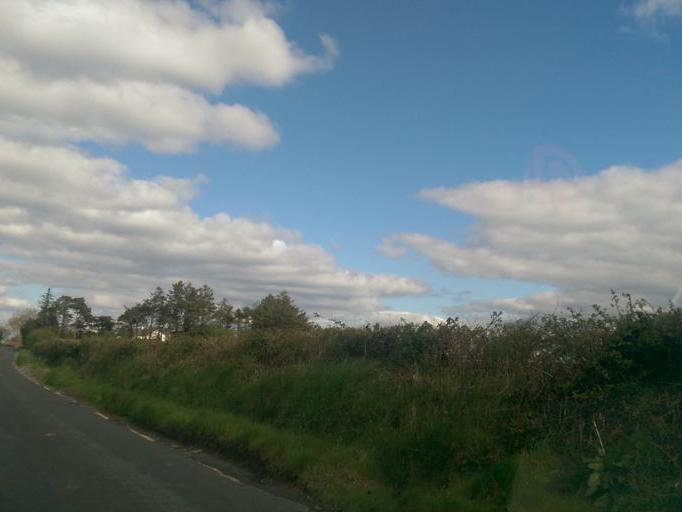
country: IE
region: Connaught
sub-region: County Galway
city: Loughrea
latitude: 53.4248
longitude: -8.5043
